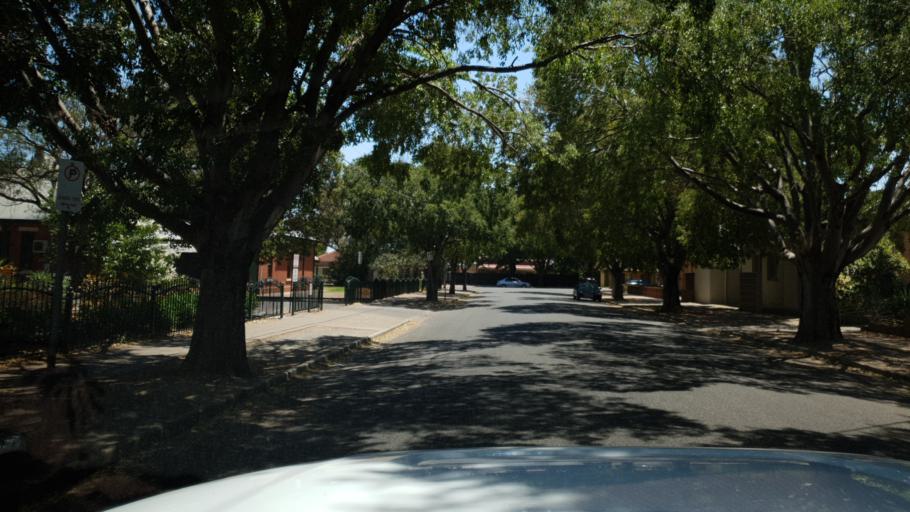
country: AU
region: South Australia
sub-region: Mitcham
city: Clarence Gardens
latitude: -34.9788
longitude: 138.5793
